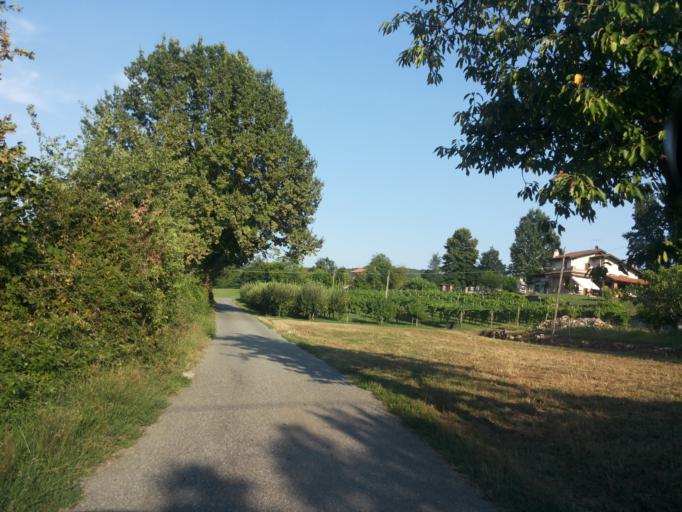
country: IT
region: Piedmont
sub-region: Provincia di Biella
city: Roppolo
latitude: 45.4044
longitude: 8.0574
